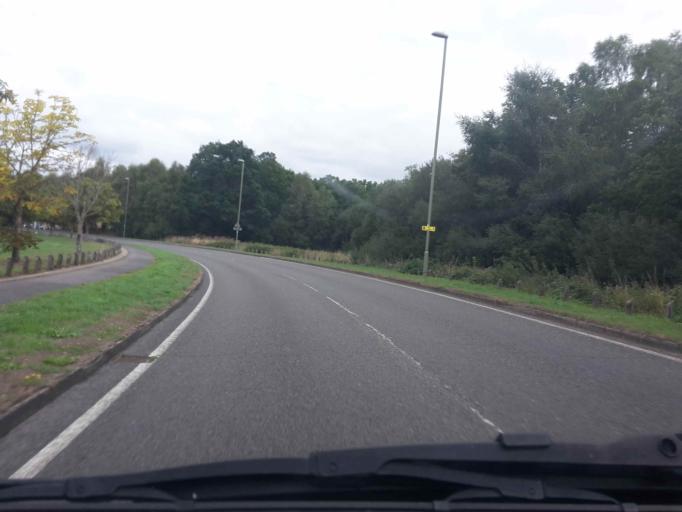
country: GB
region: England
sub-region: Hampshire
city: Fleet
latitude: 51.2950
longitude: -0.8209
